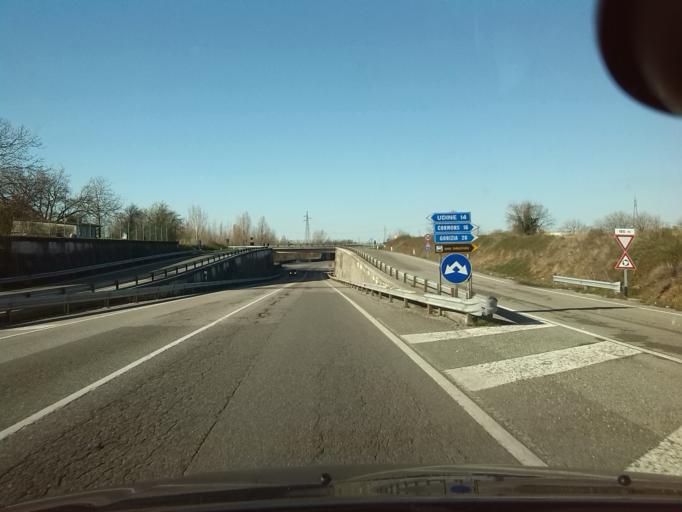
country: IT
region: Friuli Venezia Giulia
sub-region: Provincia di Udine
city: Cividale del Friuli
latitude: 46.0878
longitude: 13.4069
